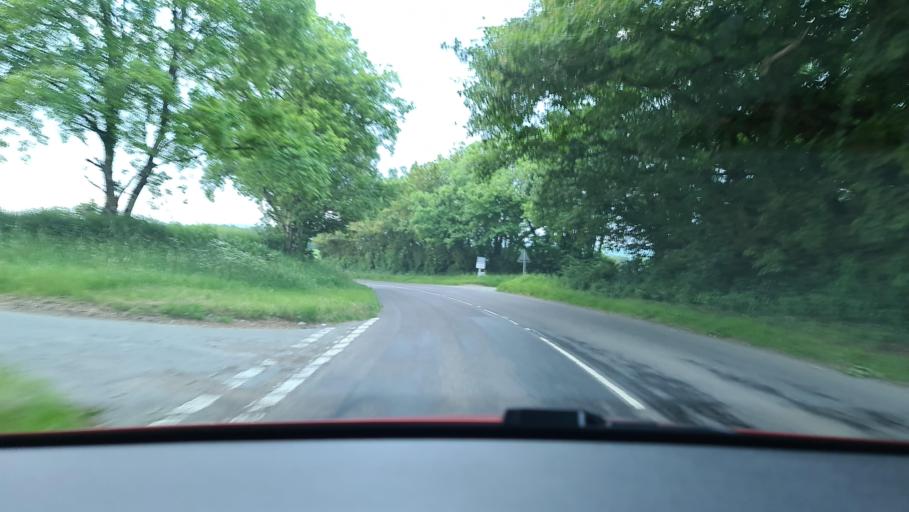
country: GB
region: England
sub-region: Cornwall
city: Looe
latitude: 50.4051
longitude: -4.4240
